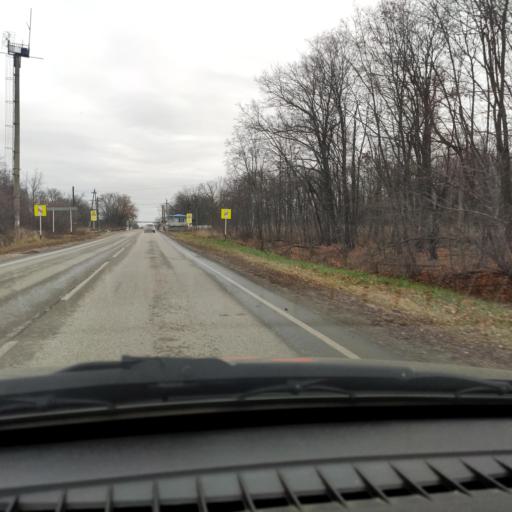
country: RU
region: Samara
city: Zhigulevsk
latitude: 53.3408
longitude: 49.4640
